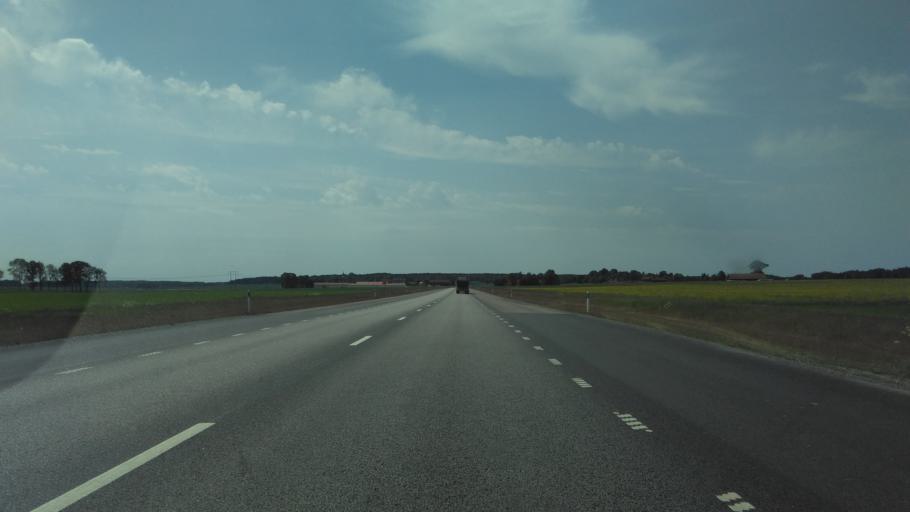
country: SE
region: Vaestra Goetaland
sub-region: Lidkopings Kommun
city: Lidkoping
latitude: 58.4694
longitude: 13.0564
